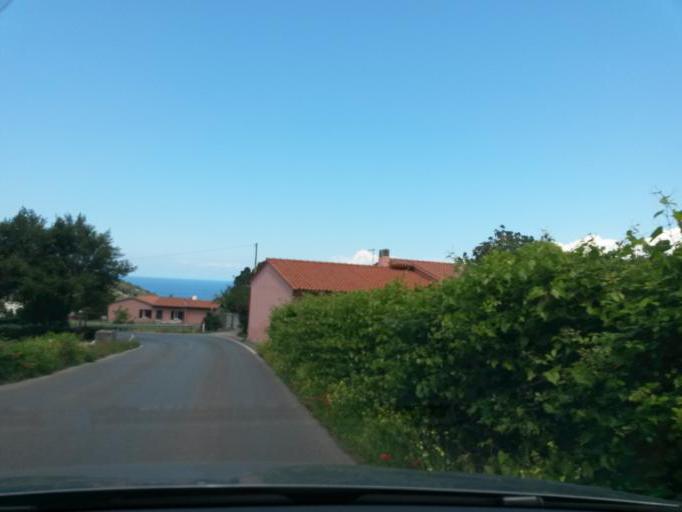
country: IT
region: Tuscany
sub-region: Provincia di Livorno
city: Marciana Marina
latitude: 42.7974
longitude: 10.1915
